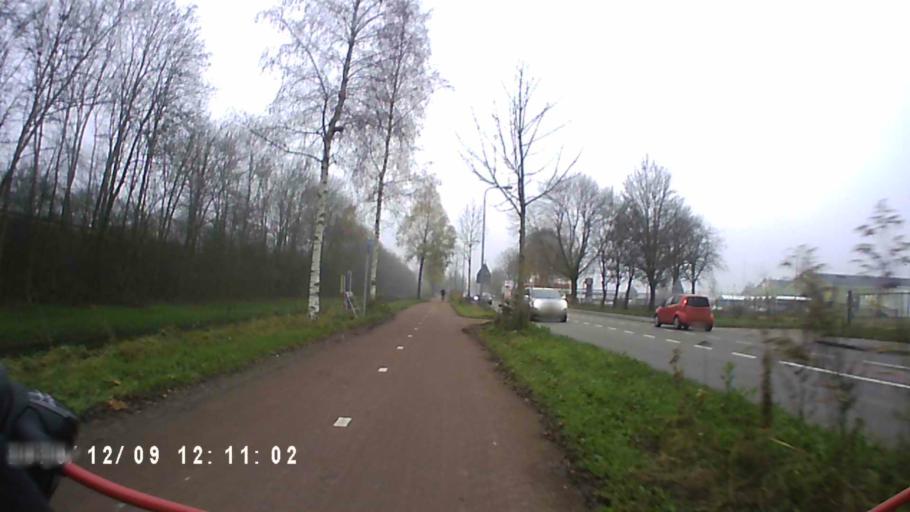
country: NL
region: Groningen
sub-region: Gemeente Groningen
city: Oosterpark
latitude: 53.2048
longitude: 6.6003
